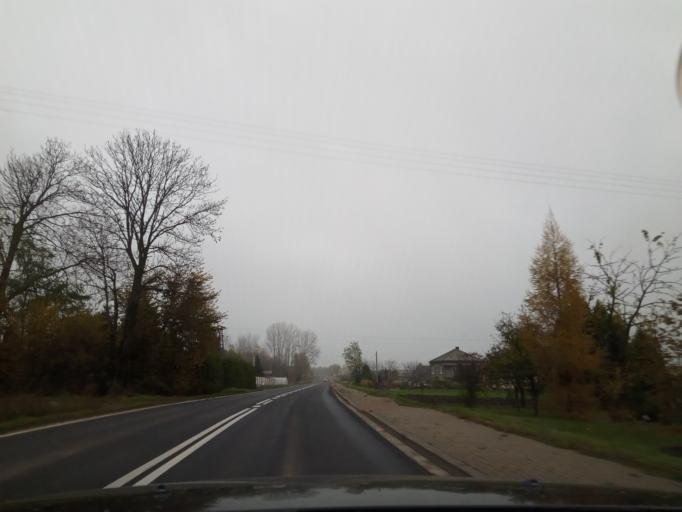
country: PL
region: Lesser Poland Voivodeship
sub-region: Powiat proszowicki
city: Proszowice
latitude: 50.1679
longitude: 20.2159
